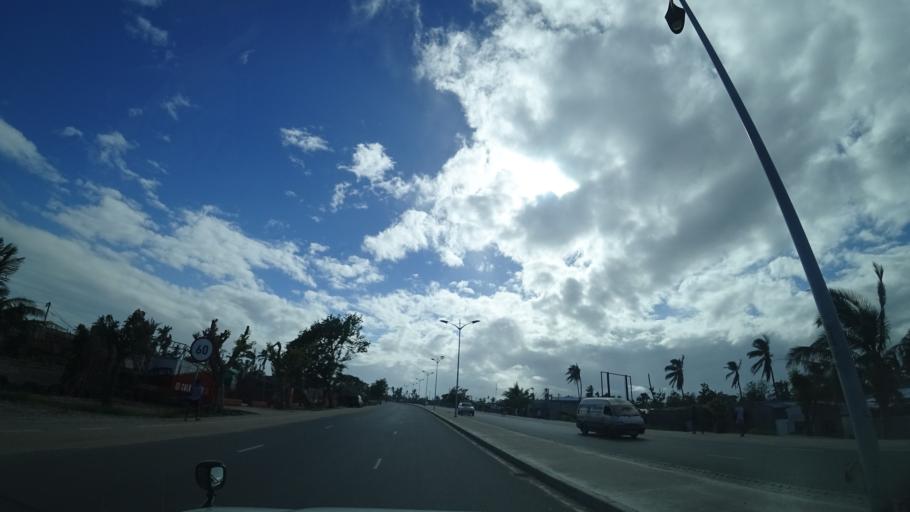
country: MZ
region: Sofala
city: Beira
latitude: -19.7790
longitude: 34.8811
